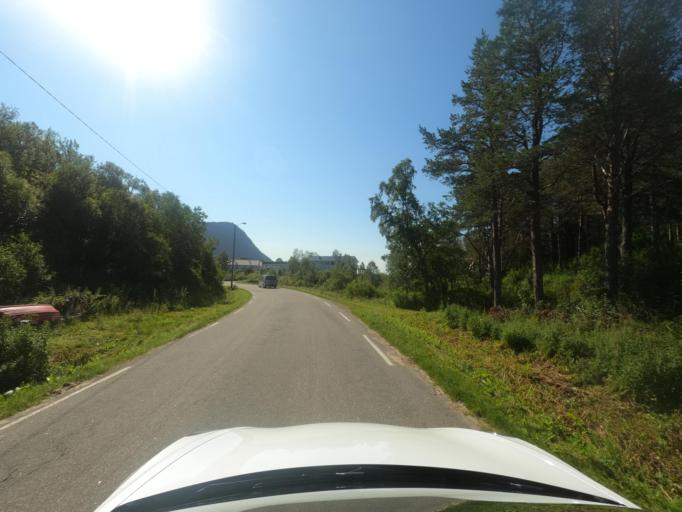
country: NO
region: Nordland
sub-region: Hadsel
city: Stokmarknes
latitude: 68.3117
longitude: 14.9868
